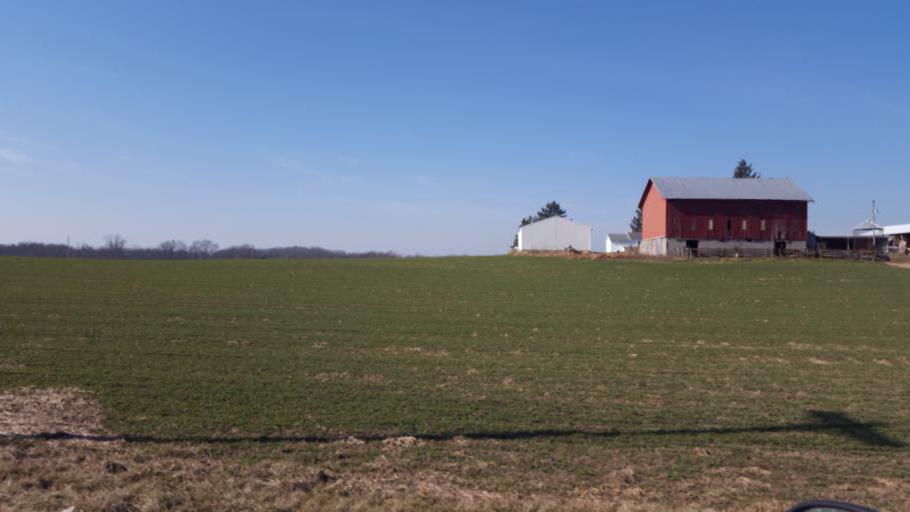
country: US
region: Ohio
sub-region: Wayne County
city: Shreve
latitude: 40.6791
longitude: -82.0530
